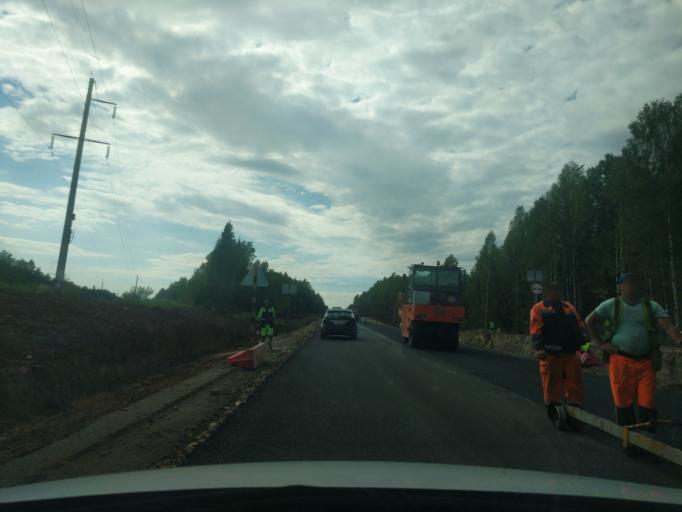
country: RU
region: Kostroma
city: Sudislavl'
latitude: 57.8485
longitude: 41.5886
